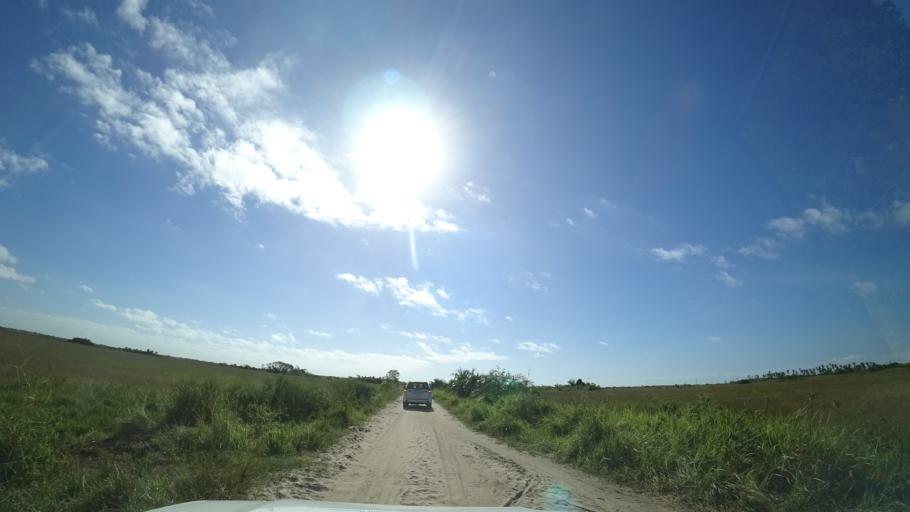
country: MZ
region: Sofala
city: Beira
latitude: -19.7120
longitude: 35.0144
